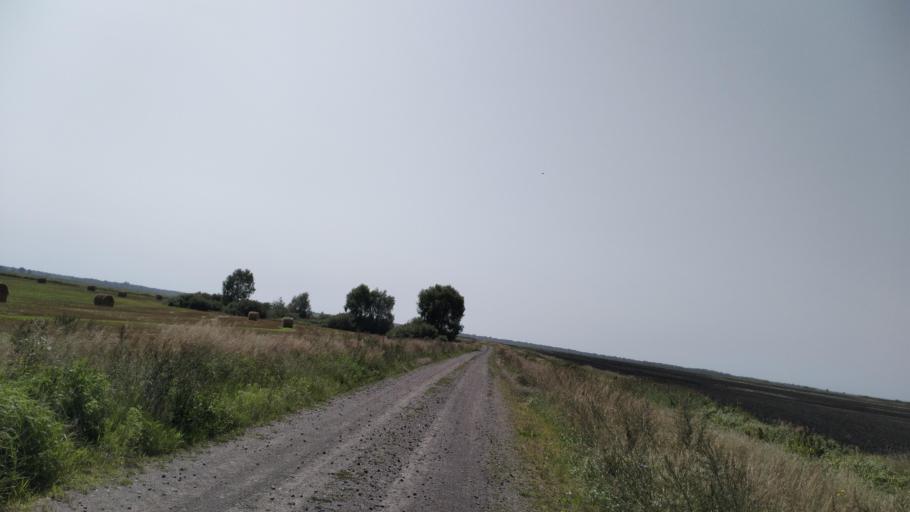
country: BY
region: Brest
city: Davyd-Haradok
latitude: 51.9989
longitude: 27.1652
